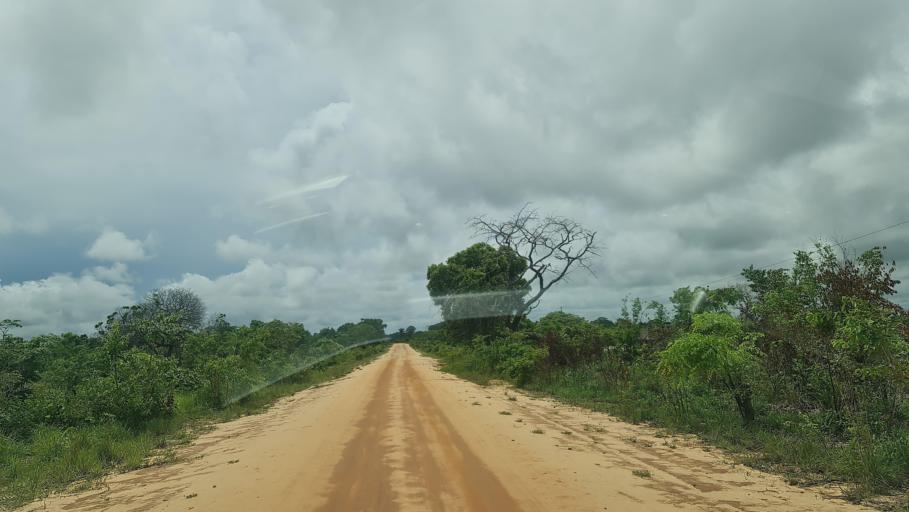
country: MZ
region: Zambezia
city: Quelimane
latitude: -17.2639
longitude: 37.2382
